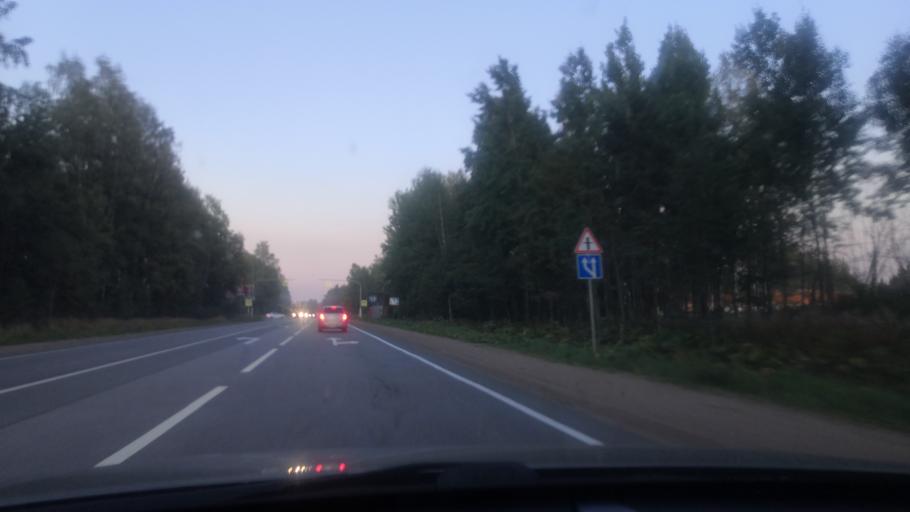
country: RU
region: St.-Petersburg
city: Beloostrov
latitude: 60.1984
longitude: 30.0043
